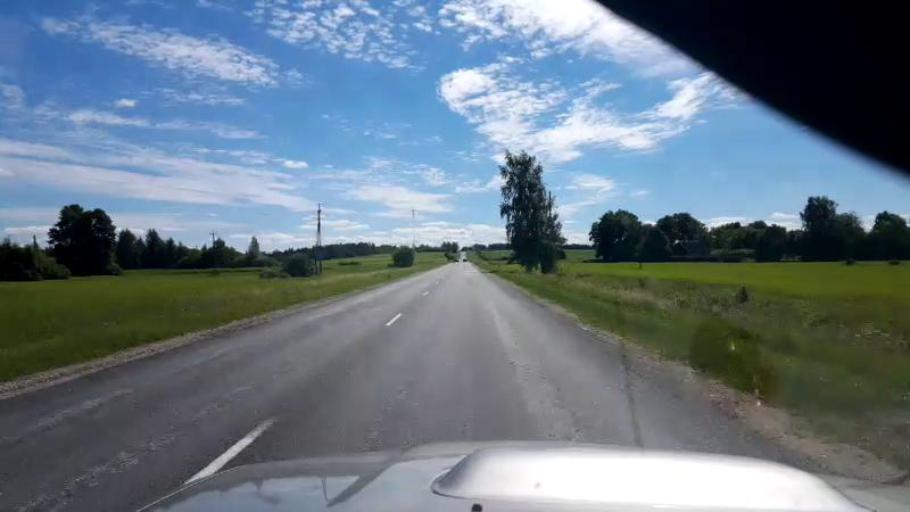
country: EE
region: Laeaene-Virumaa
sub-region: Rakke vald
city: Rakke
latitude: 58.8605
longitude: 26.2932
